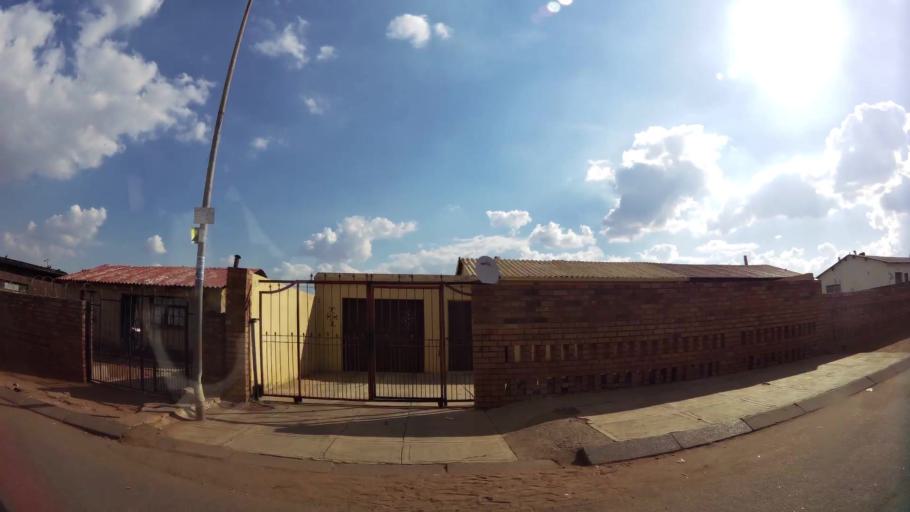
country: ZA
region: Gauteng
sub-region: City of Johannesburg Metropolitan Municipality
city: Soweto
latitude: -26.2198
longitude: 27.8598
